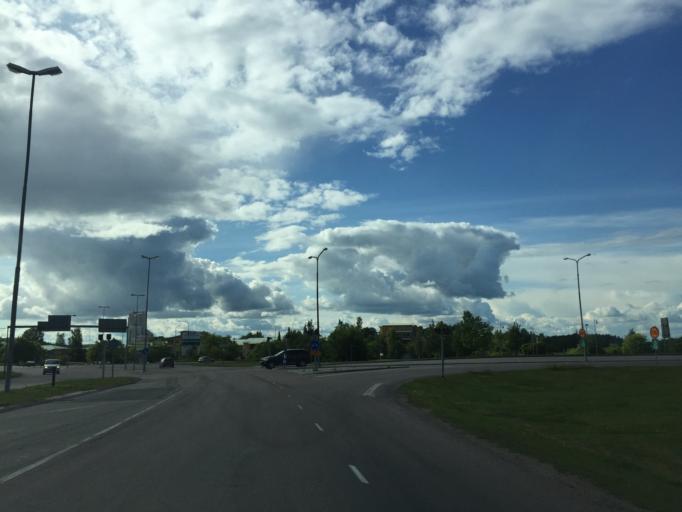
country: SE
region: Vaestmanland
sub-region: Vasteras
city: Vasteras
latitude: 59.6196
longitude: 16.5150
